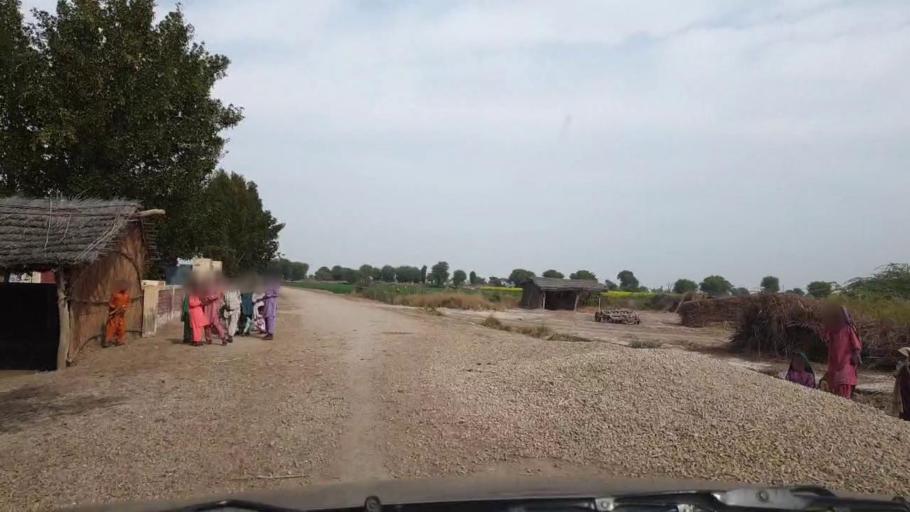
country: PK
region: Sindh
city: Sanghar
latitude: 26.0964
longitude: 68.8814
